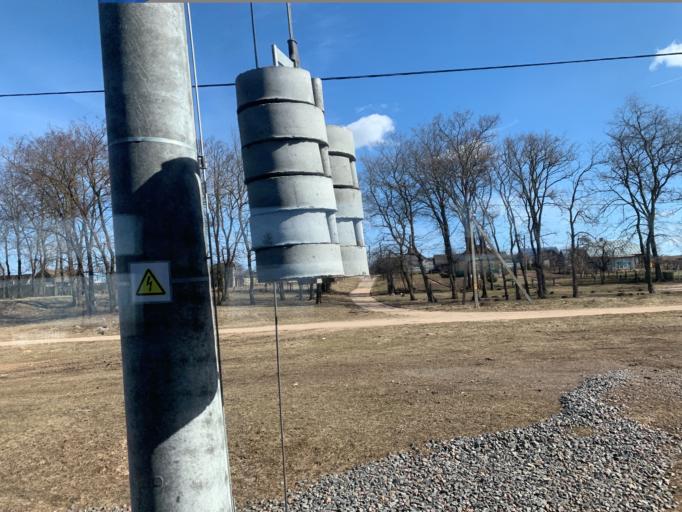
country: BY
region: Minsk
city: Haradzyeya
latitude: 53.3219
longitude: 26.5429
